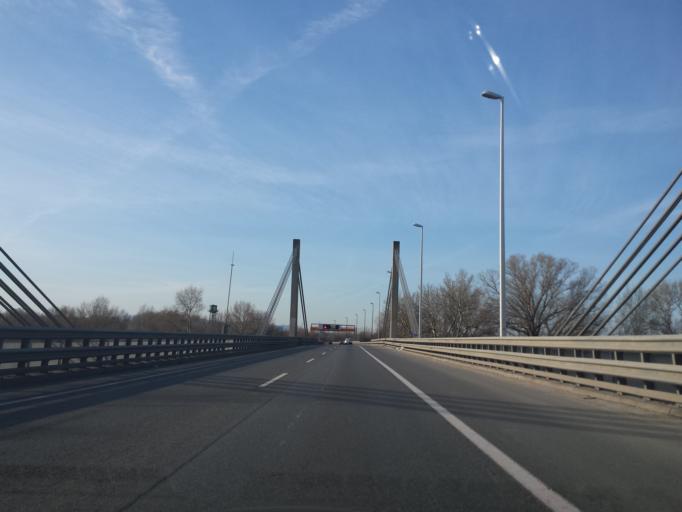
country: AT
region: Lower Austria
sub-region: Politischer Bezirk Wien-Umgebung
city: Schwechat
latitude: 48.1805
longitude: 16.4515
